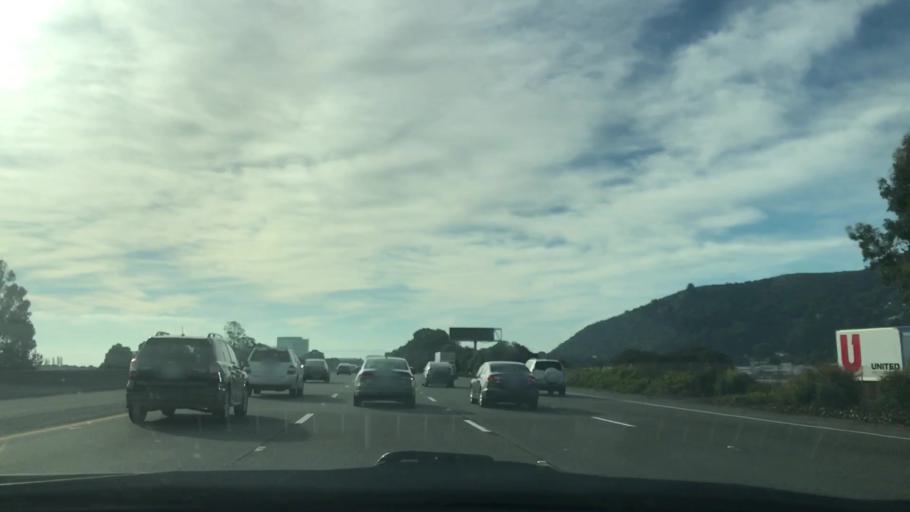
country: US
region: California
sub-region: San Mateo County
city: Brisbane
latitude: 37.6875
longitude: -122.3910
